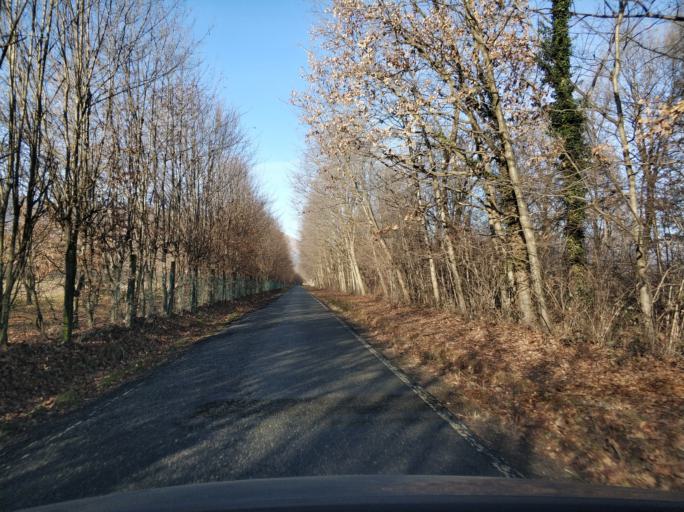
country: IT
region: Piedmont
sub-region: Provincia di Torino
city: Fiano
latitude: 45.2176
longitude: 7.5456
